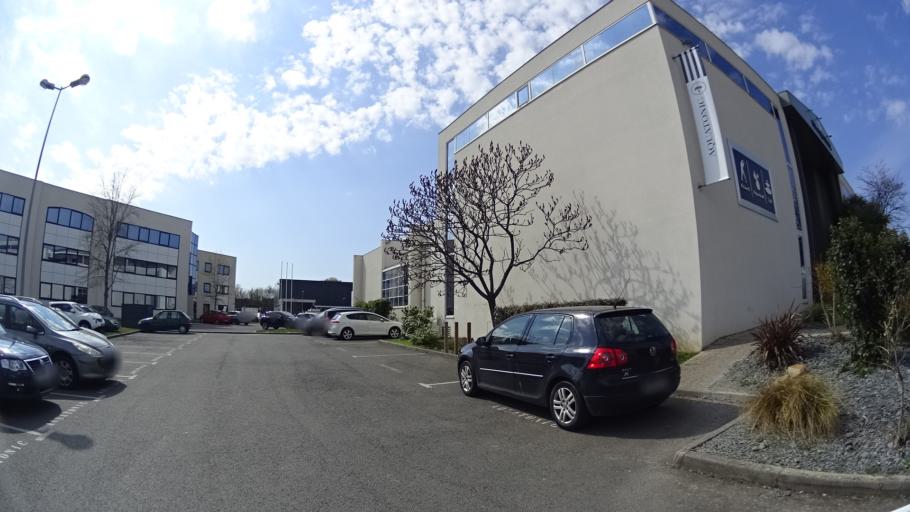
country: FR
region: Brittany
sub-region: Departement d'Ille-et-Vilaine
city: Saint-Gregoire
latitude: 48.1542
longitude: -1.6951
